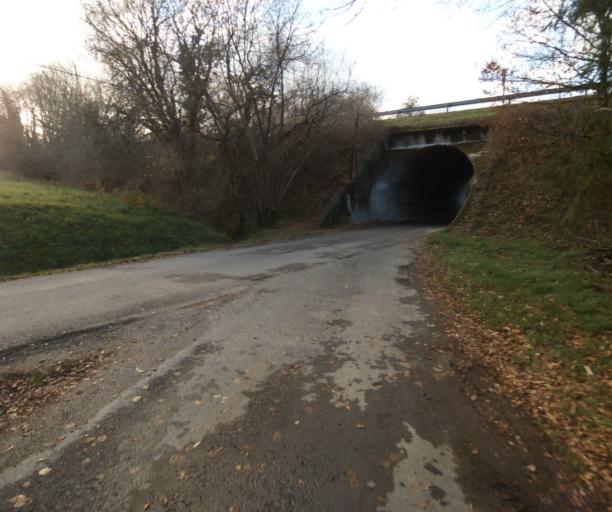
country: FR
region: Limousin
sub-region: Departement de la Correze
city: Laguenne
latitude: 45.2342
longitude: 1.7699
